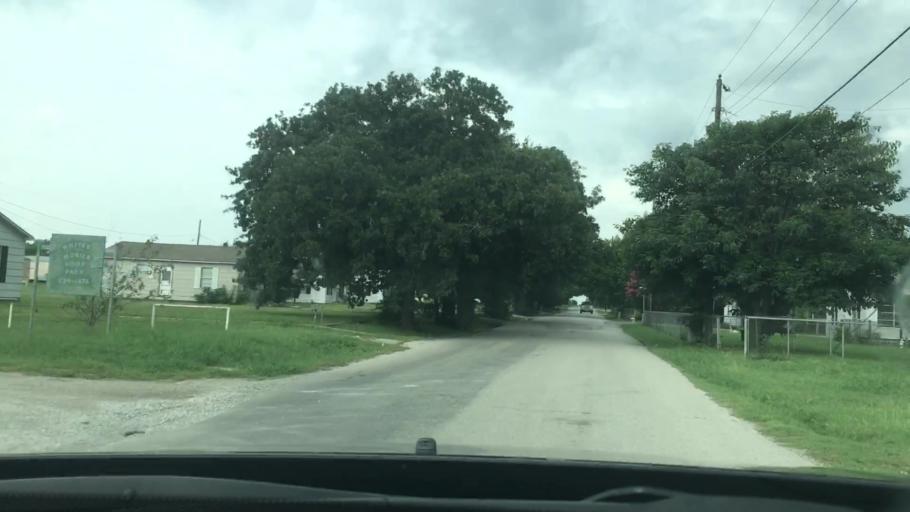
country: US
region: Oklahoma
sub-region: Carter County
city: Healdton
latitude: 34.2165
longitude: -97.4770
